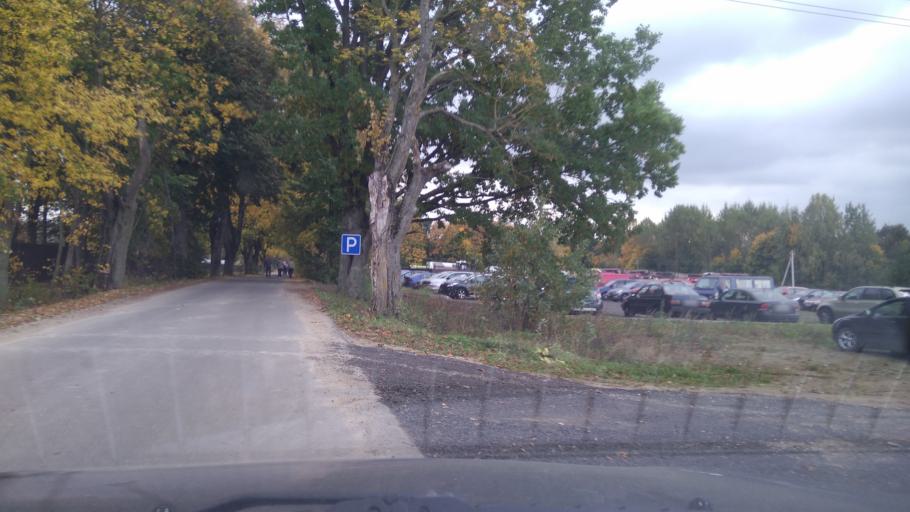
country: BY
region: Minsk
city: Dukora
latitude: 53.6775
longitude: 27.9622
